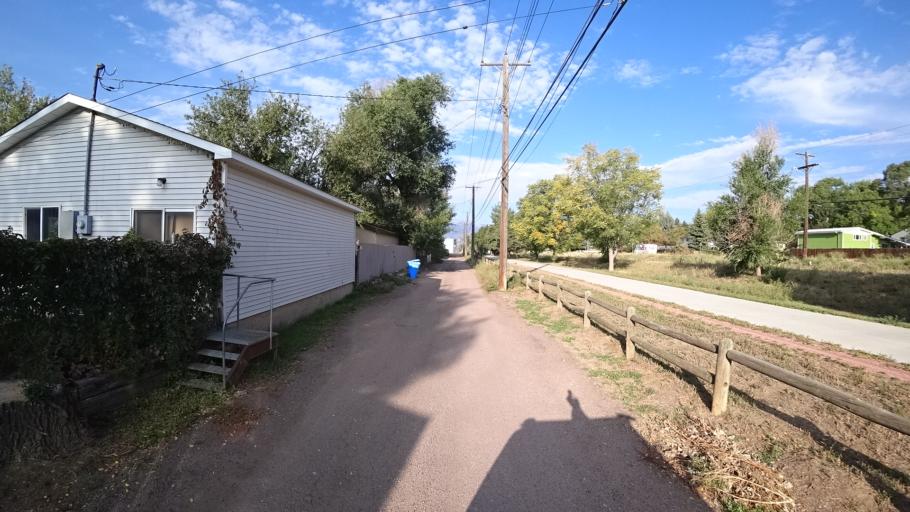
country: US
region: Colorado
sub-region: El Paso County
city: Colorado Springs
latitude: 38.8589
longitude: -104.7708
